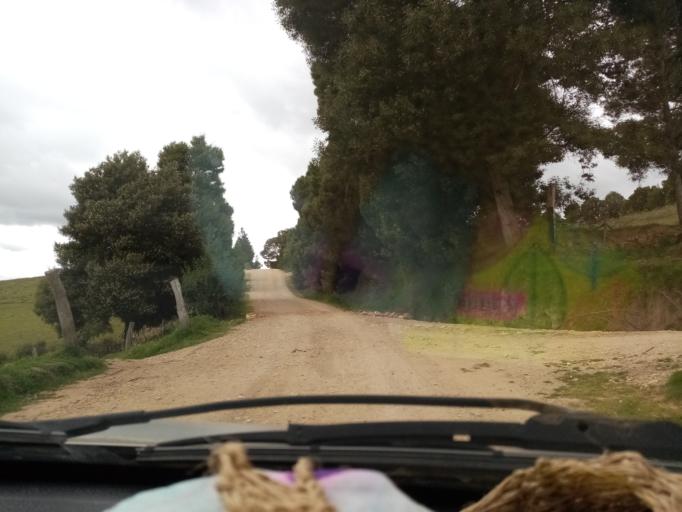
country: CO
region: Boyaca
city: Toca
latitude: 5.6067
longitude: -73.2357
